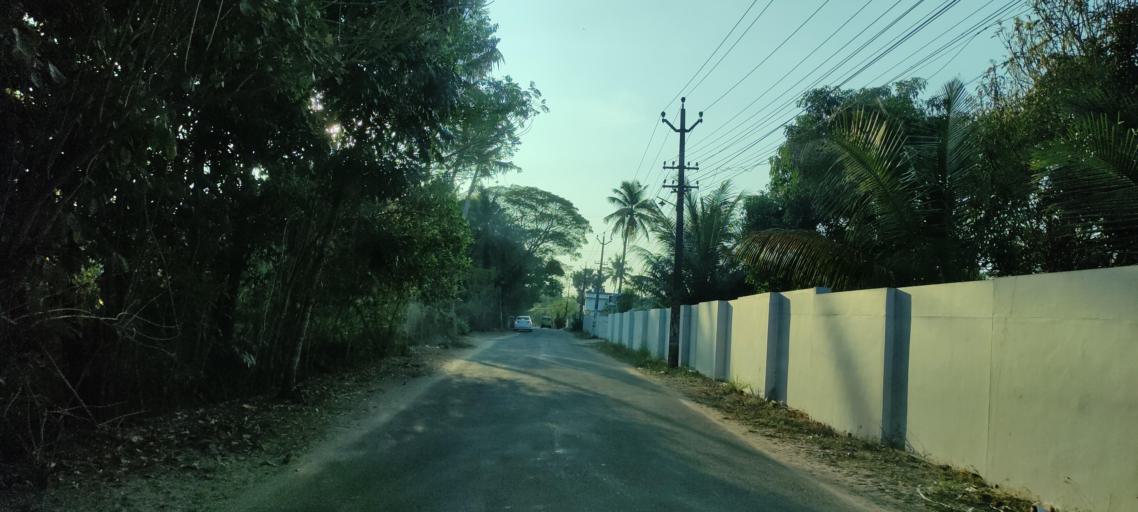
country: IN
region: Kerala
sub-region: Alappuzha
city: Vayalar
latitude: 9.7248
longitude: 76.3594
